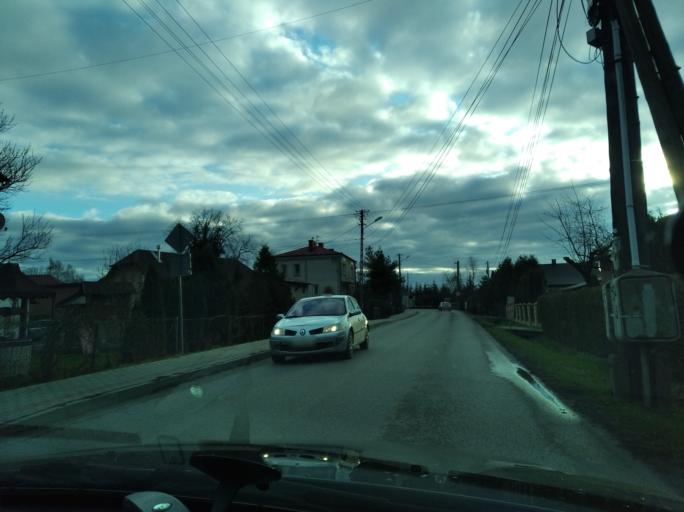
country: PL
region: Subcarpathian Voivodeship
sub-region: Powiat rzeszowski
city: Krasne
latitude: 50.0697
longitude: 22.1203
